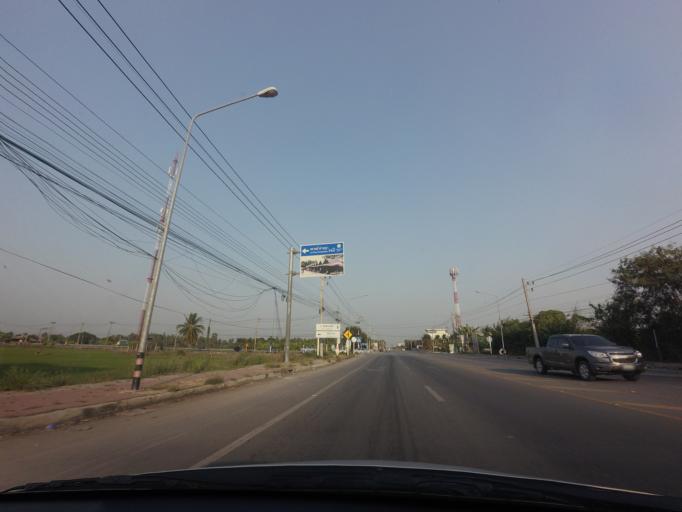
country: TH
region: Nakhon Pathom
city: Nakhon Chai Si
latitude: 13.8043
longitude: 100.2229
